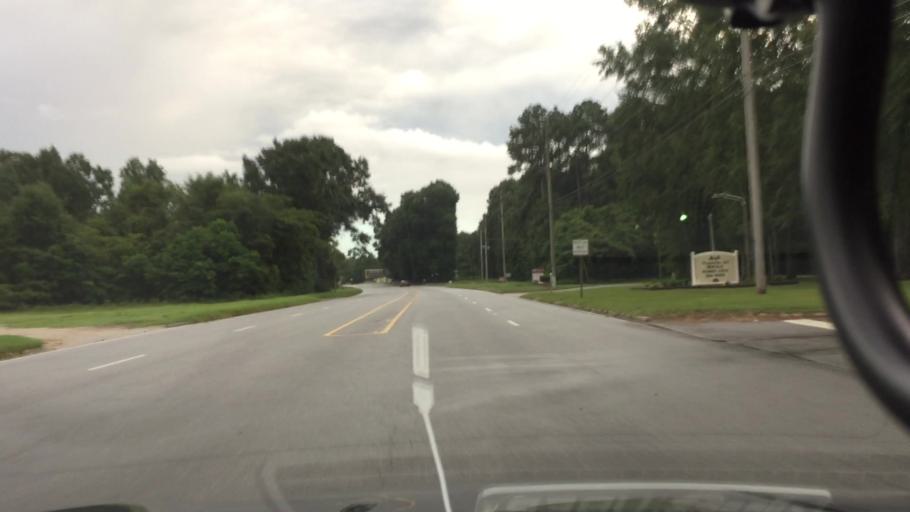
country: US
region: Alabama
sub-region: Pike County
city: Troy
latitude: 31.7596
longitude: -85.9614
